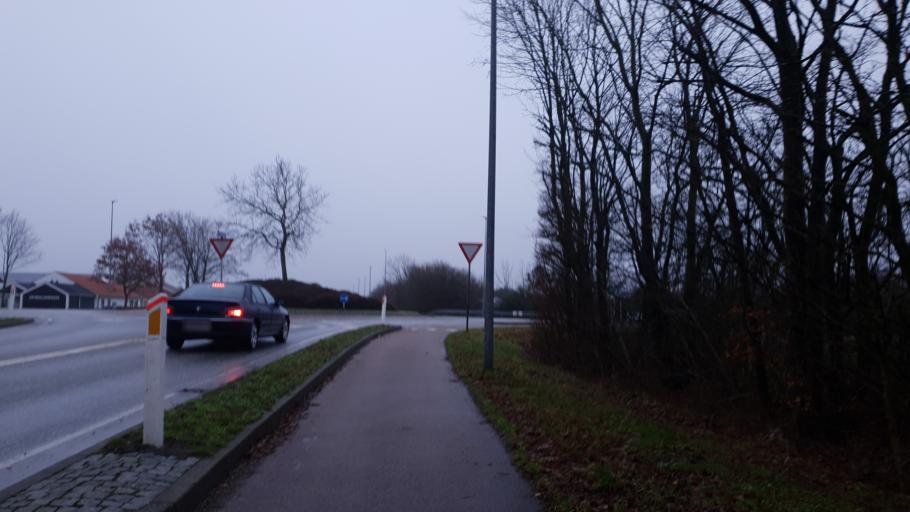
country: DK
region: Central Jutland
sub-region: Hedensted Kommune
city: Hedensted
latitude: 55.7816
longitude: 9.6968
